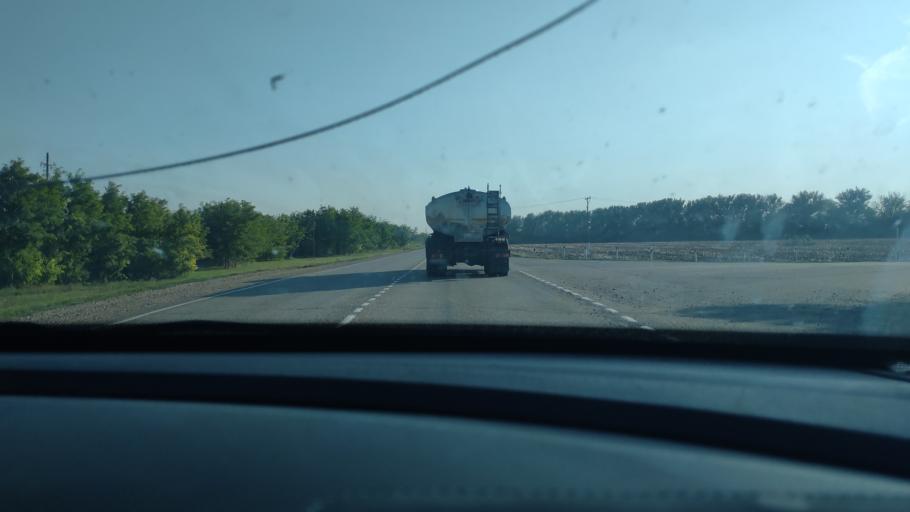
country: RU
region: Krasnodarskiy
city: Starominskaya
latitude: 46.4486
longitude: 39.0284
